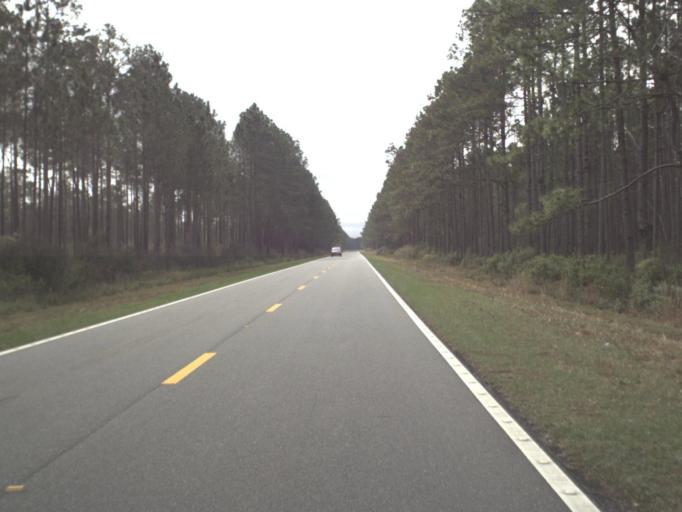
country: US
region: Florida
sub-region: Gulf County
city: Wewahitchka
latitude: 30.0972
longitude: -84.9852
